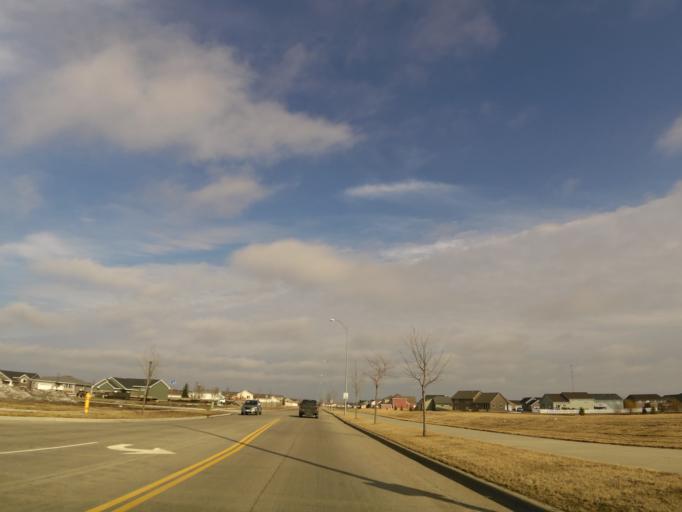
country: US
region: North Dakota
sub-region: Grand Forks County
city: Grand Forks
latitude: 47.8821
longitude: -97.0662
